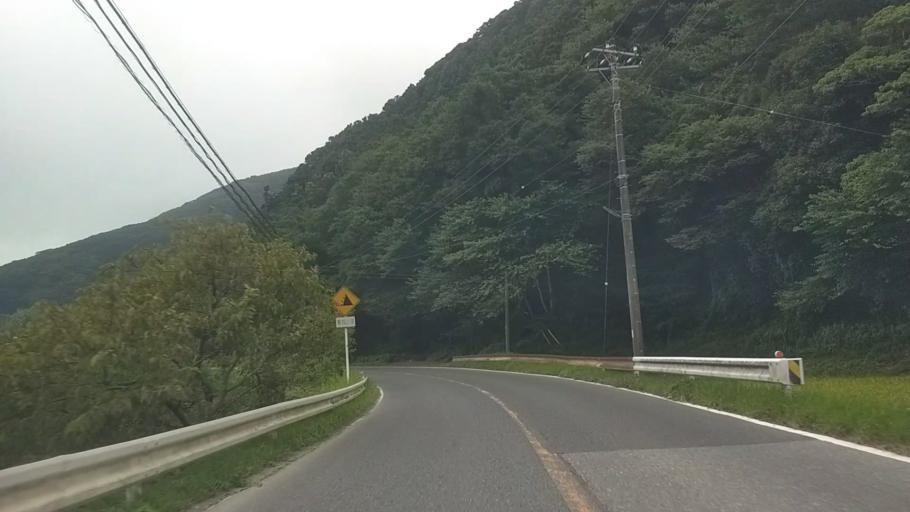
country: JP
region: Chiba
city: Tateyama
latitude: 35.1447
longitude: 139.8624
